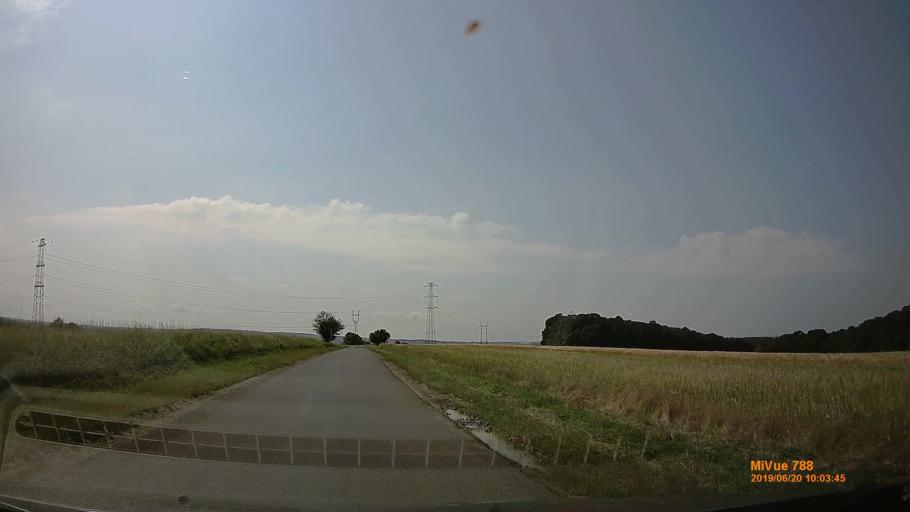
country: HU
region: Baranya
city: Mecseknadasd
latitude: 46.1954
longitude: 18.4622
